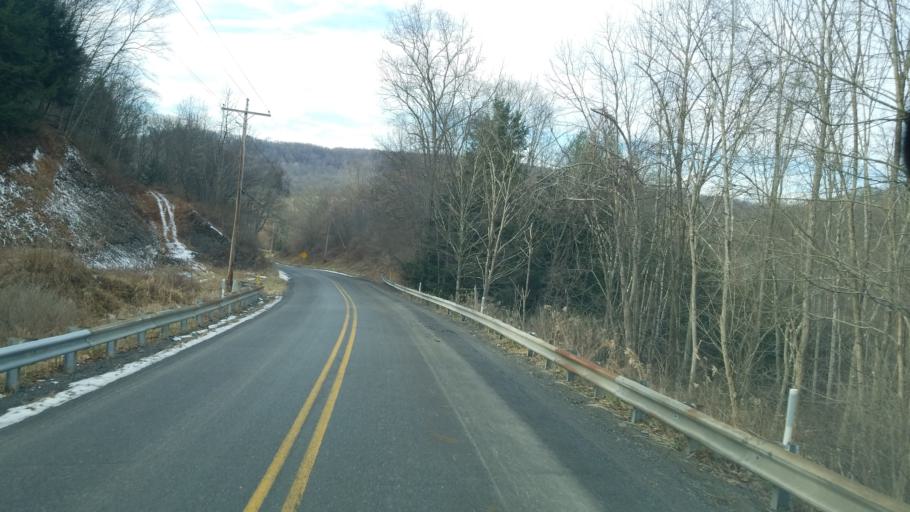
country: US
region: Pennsylvania
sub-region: Jefferson County
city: Punxsutawney
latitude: 40.8340
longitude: -79.1060
